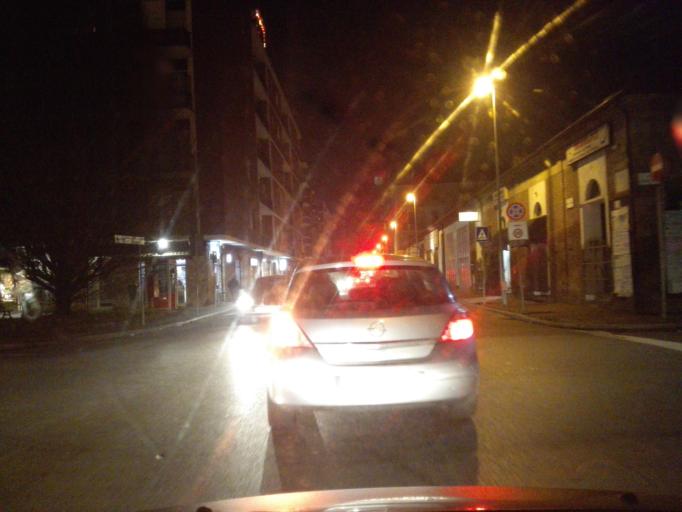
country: IT
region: Piedmont
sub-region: Provincia di Alessandria
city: Alessandria
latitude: 44.9022
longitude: 8.6080
